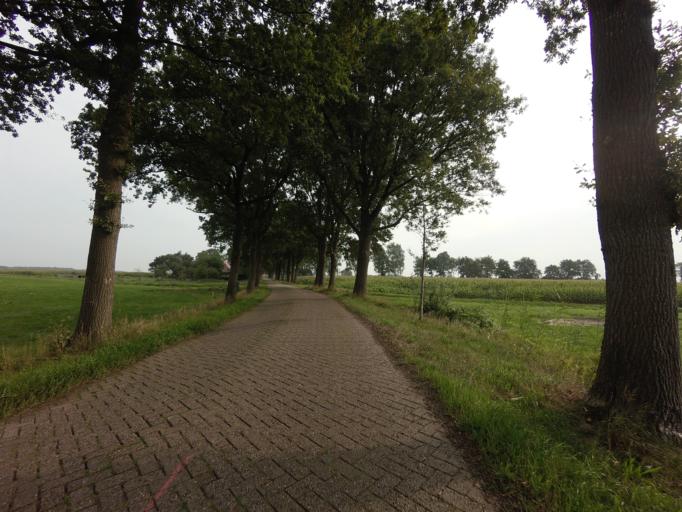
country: NL
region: Drenthe
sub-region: Gemeente Westerveld
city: Dwingeloo
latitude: 52.8642
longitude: 6.4224
